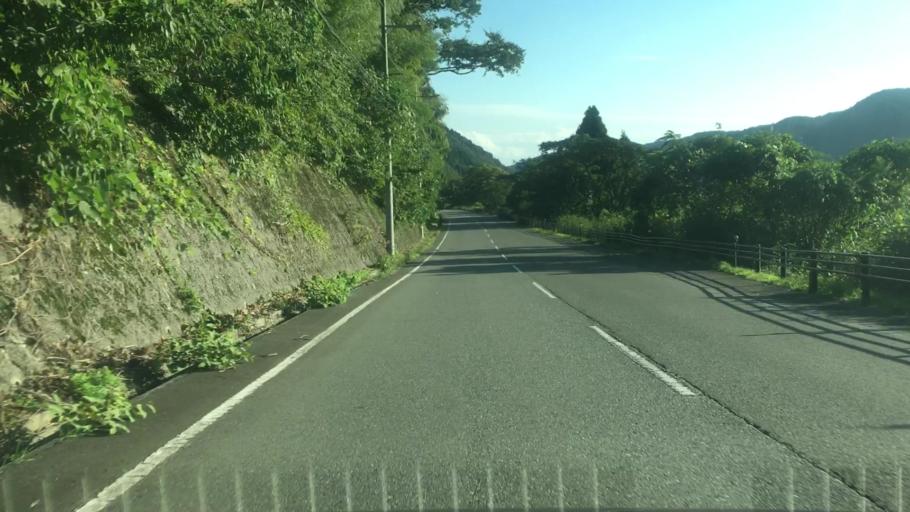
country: JP
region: Hyogo
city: Toyooka
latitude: 35.6040
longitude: 134.8060
